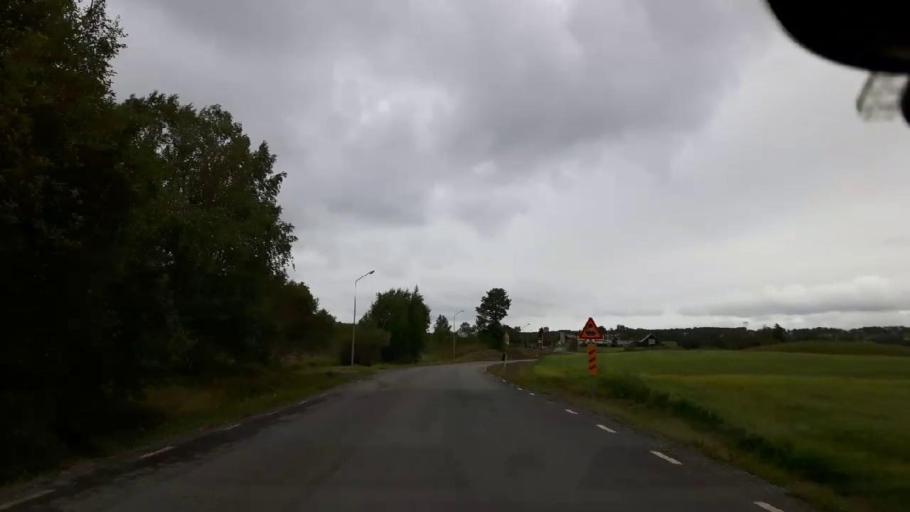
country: SE
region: Jaemtland
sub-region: OEstersunds Kommun
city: Ostersund
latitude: 62.9973
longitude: 14.5786
